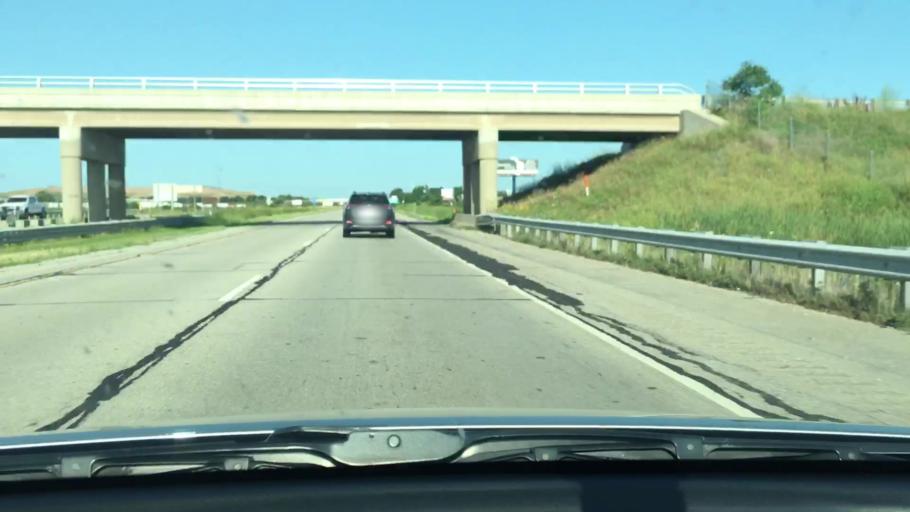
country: US
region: Wisconsin
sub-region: Outagamie County
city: Little Chute
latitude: 44.2980
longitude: -88.3225
